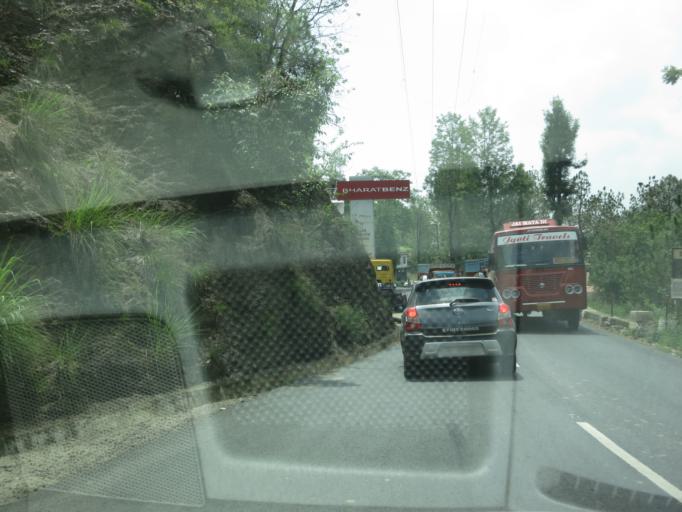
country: IN
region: Himachal Pradesh
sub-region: Solan
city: Dagshai
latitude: 30.8988
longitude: 77.0673
